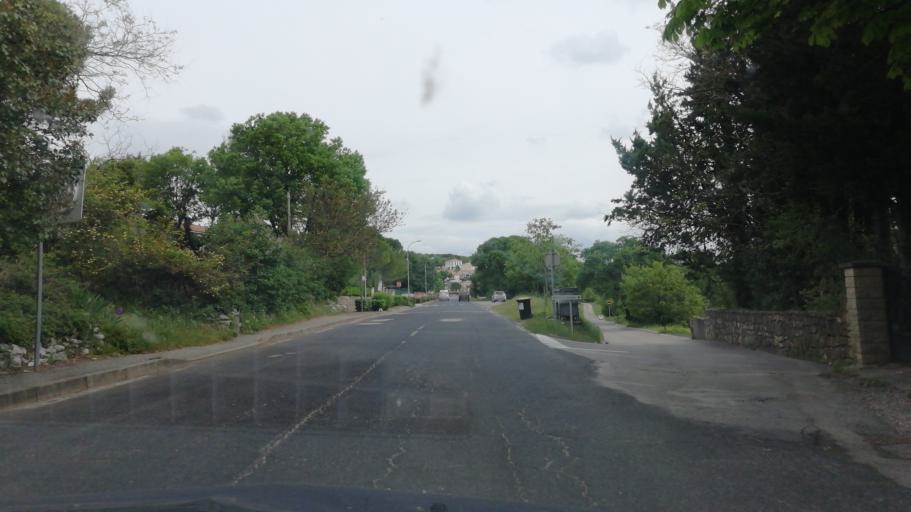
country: FR
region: Languedoc-Roussillon
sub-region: Departement de l'Herault
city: Saint-Martin-de-Londres
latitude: 43.7947
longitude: 3.7336
